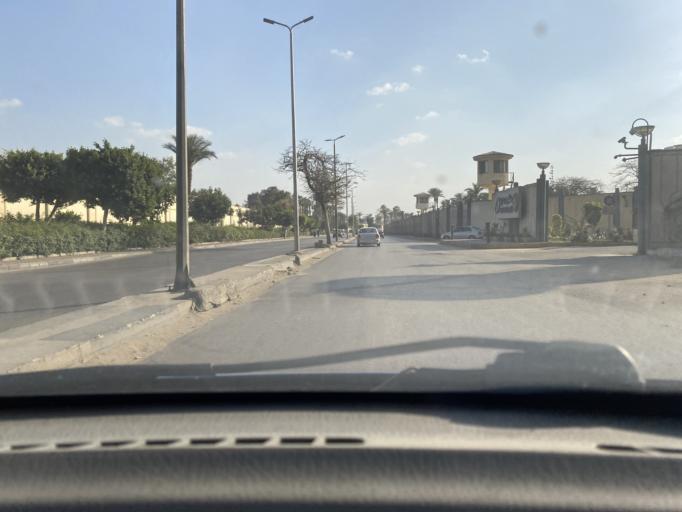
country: EG
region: Muhafazat al Qahirah
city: Cairo
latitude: 30.0990
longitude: 31.2995
